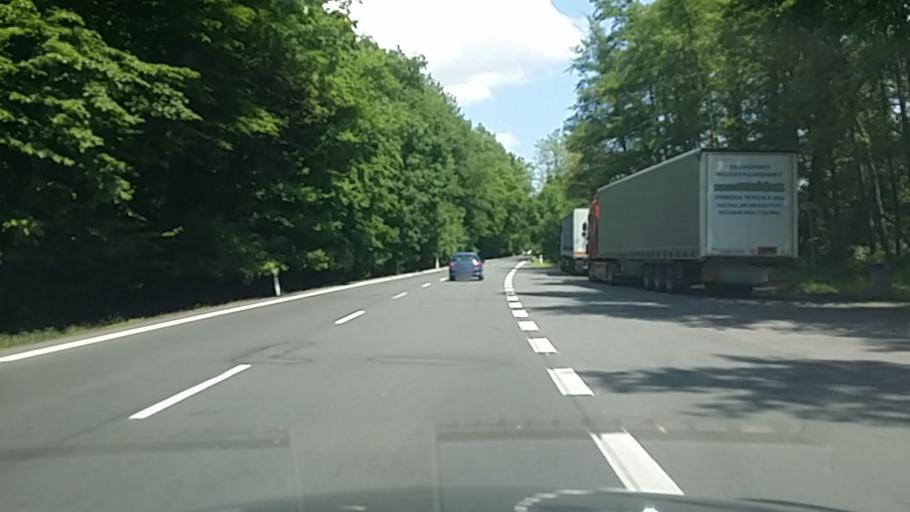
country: SK
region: Banskobystricky
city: Dudince
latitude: 48.2382
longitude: 18.9619
